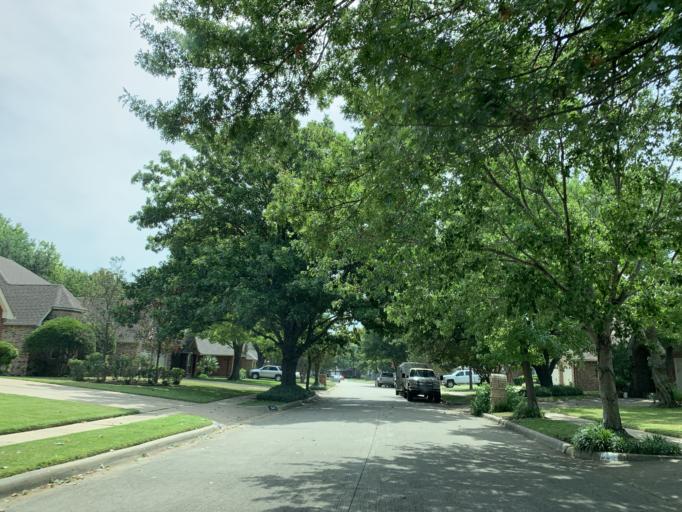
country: US
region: Texas
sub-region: Dallas County
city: Grand Prairie
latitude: 32.6666
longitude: -97.0007
